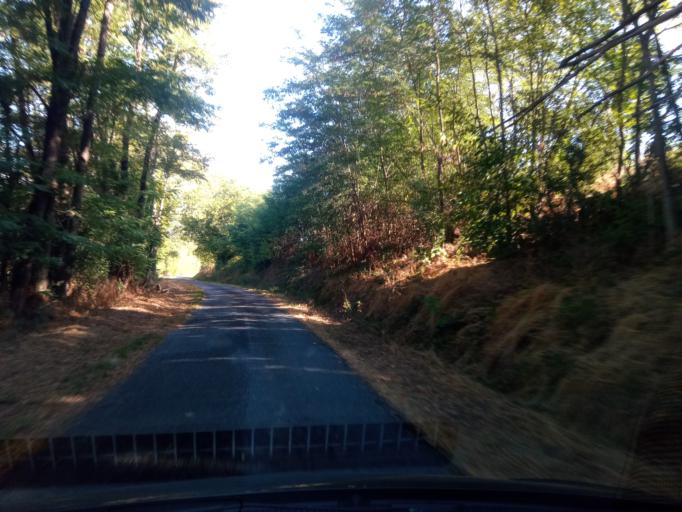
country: FR
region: Poitou-Charentes
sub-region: Departement de la Vienne
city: Saulge
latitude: 46.3755
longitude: 0.8721
